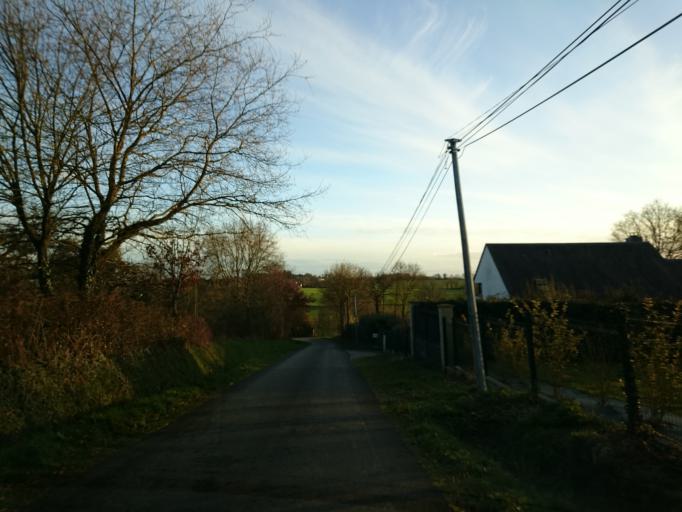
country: FR
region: Brittany
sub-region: Departement d'Ille-et-Vilaine
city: Chanteloup
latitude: 47.9259
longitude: -1.6086
